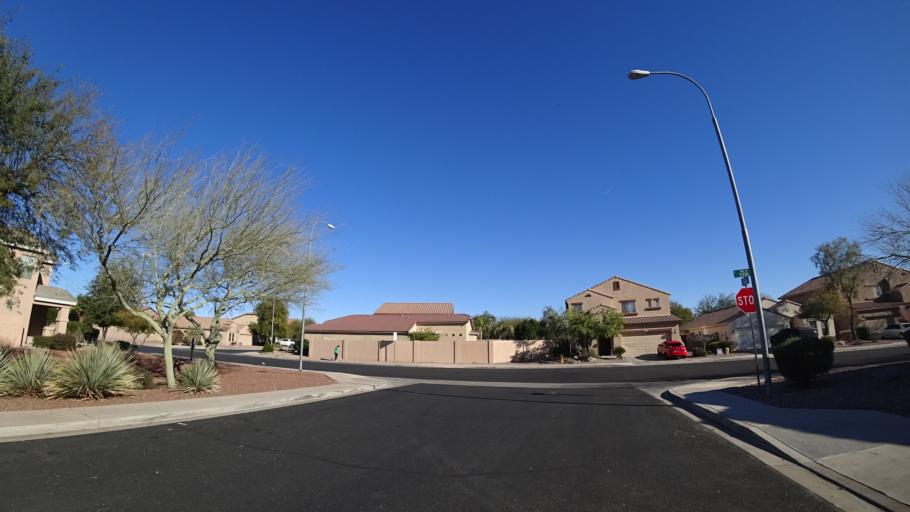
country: US
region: Arizona
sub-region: Maricopa County
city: Avondale
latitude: 33.4323
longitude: -112.3123
